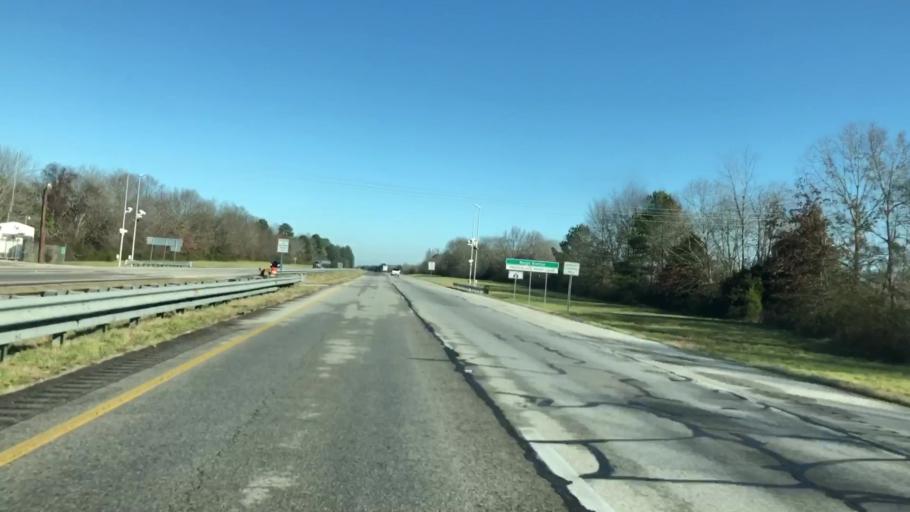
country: US
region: Alabama
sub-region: Limestone County
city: Athens
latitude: 34.8436
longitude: -86.9333
